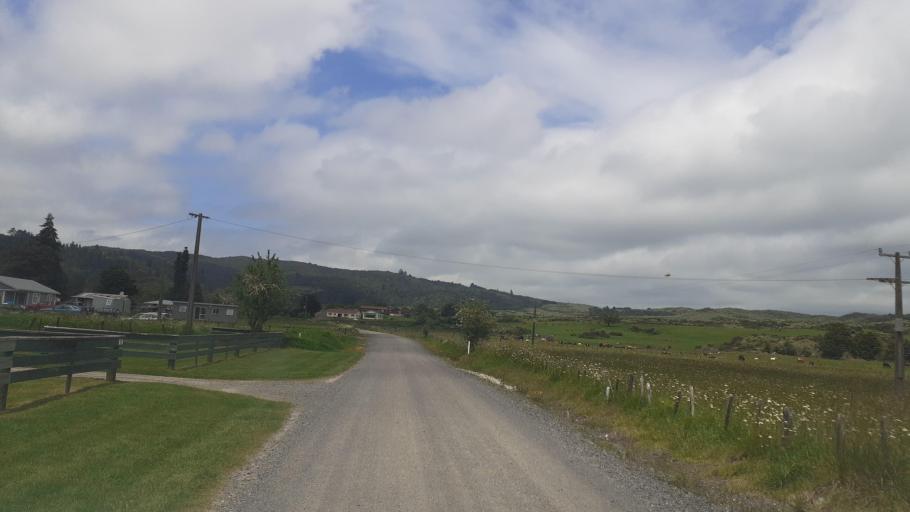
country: NZ
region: Northland
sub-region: Far North District
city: Kawakawa
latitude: -35.4203
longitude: 174.0852
